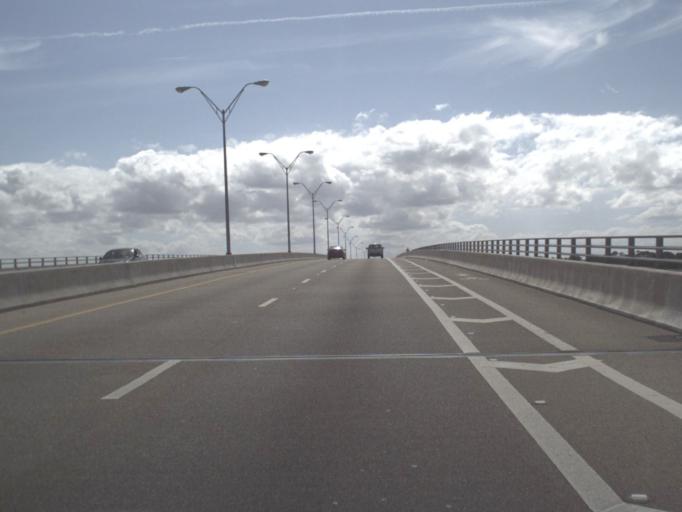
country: US
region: Florida
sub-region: Flagler County
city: Flagler Beach
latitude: 29.4786
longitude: -81.1342
